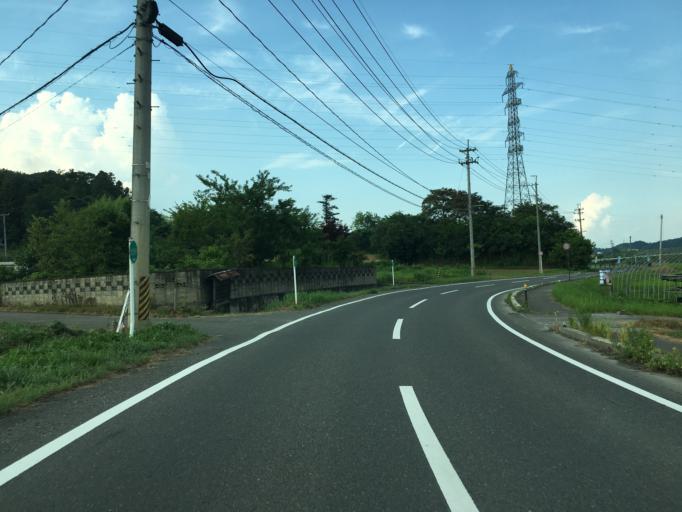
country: JP
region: Fukushima
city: Nihommatsu
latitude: 37.5664
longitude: 140.4337
